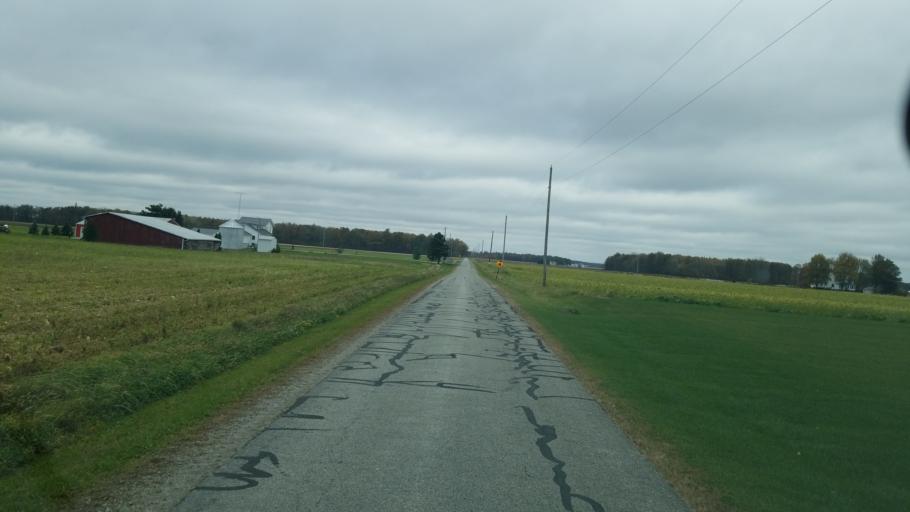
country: US
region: Ohio
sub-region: Huron County
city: Willard
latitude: 41.0194
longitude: -82.8814
